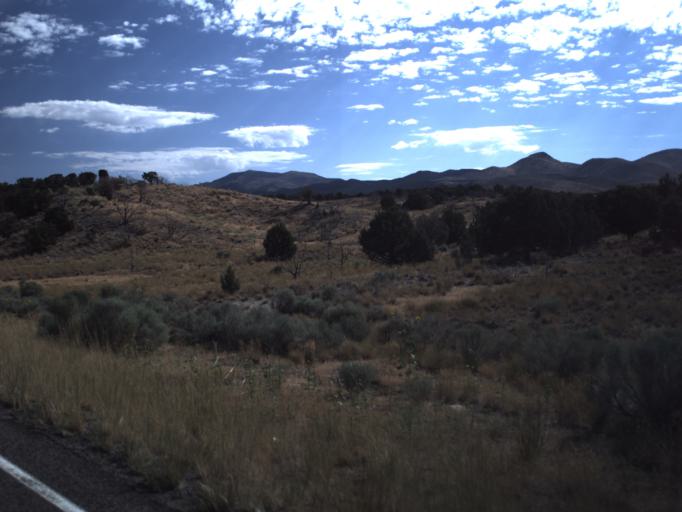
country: US
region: Utah
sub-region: Juab County
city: Mona
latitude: 39.7553
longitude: -112.1813
